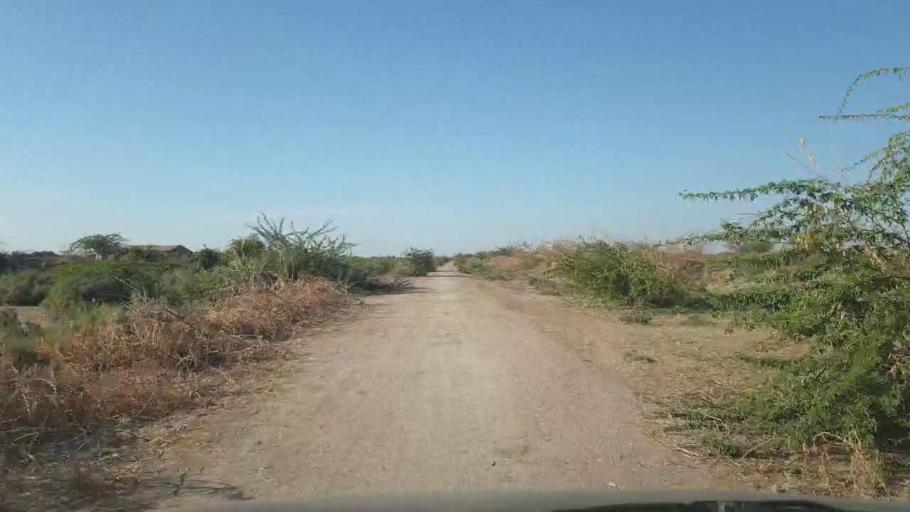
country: PK
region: Sindh
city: Dhoro Naro
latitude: 25.4312
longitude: 69.5530
